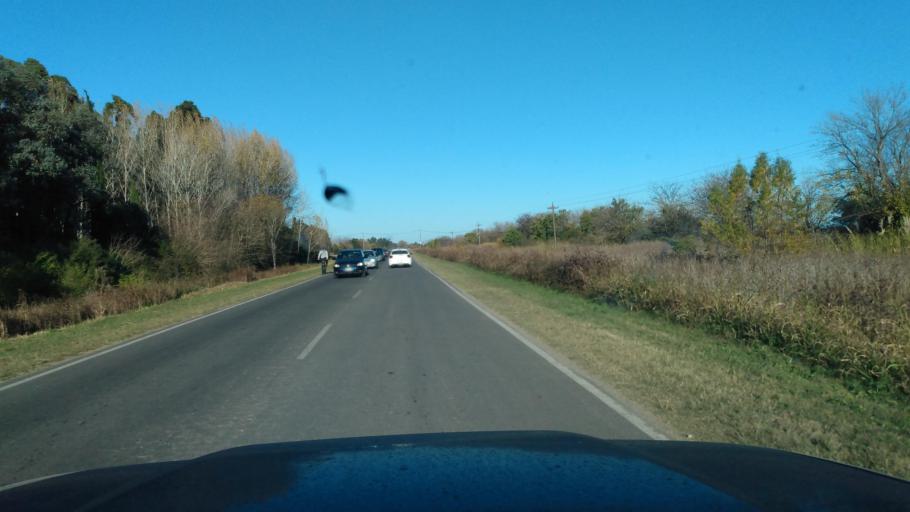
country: AR
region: Buenos Aires
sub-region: Partido de Lujan
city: Lujan
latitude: -34.4987
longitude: -59.2021
